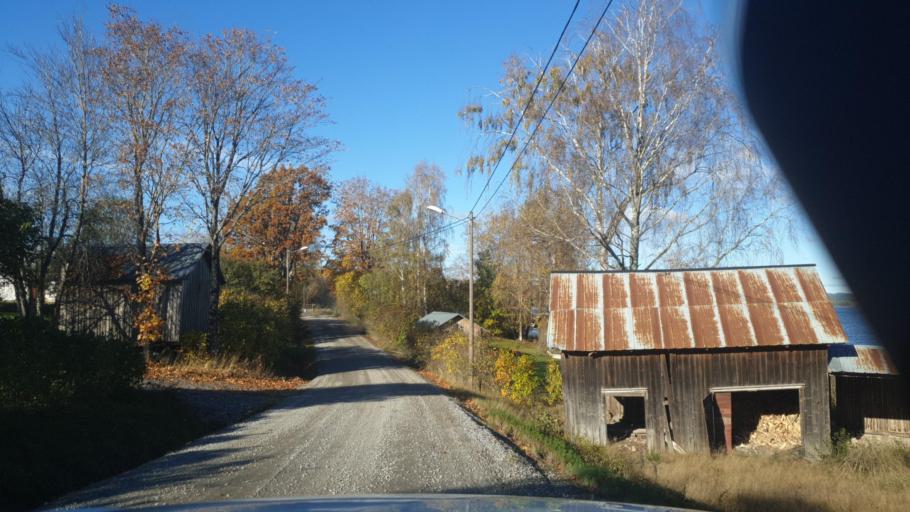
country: SE
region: Vaermland
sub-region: Karlstads Kommun
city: Edsvalla
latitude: 59.6085
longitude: 12.9169
